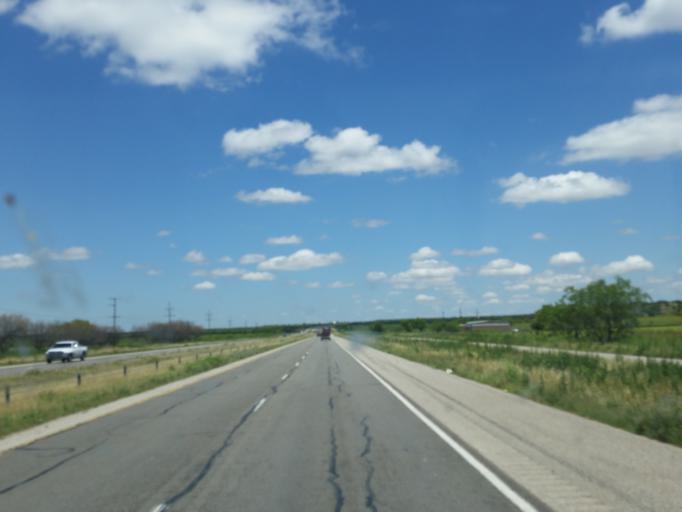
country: US
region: Texas
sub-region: Nolan County
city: Sweetwater
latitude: 32.4945
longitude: -100.2907
